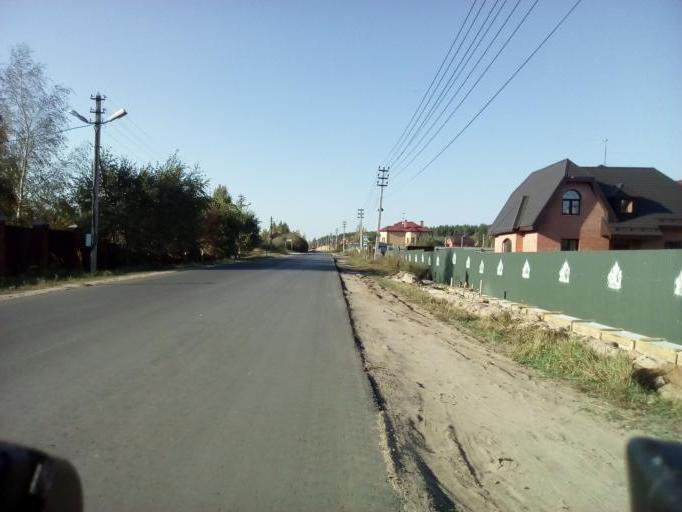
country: RU
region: Moskovskaya
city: Malyshevo
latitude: 55.5571
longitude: 38.3110
